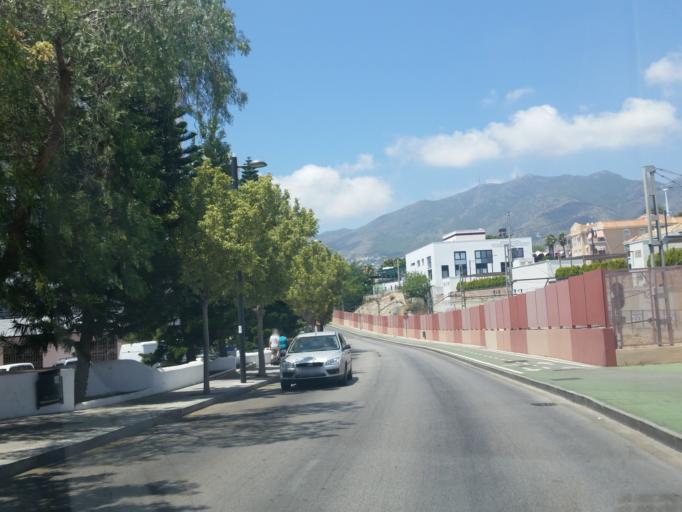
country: ES
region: Andalusia
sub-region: Provincia de Malaga
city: Benalmadena
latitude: 36.5989
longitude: -4.5371
